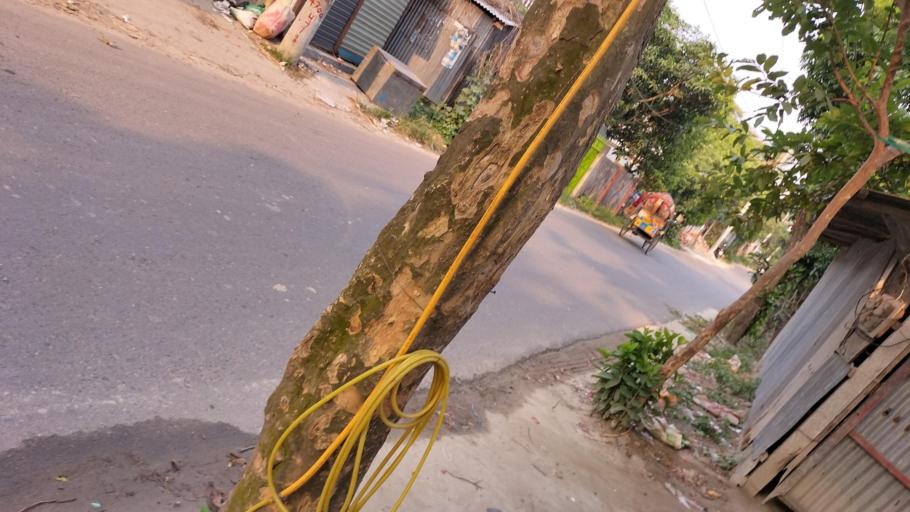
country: BD
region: Dhaka
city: Azimpur
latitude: 23.6559
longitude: 90.3389
